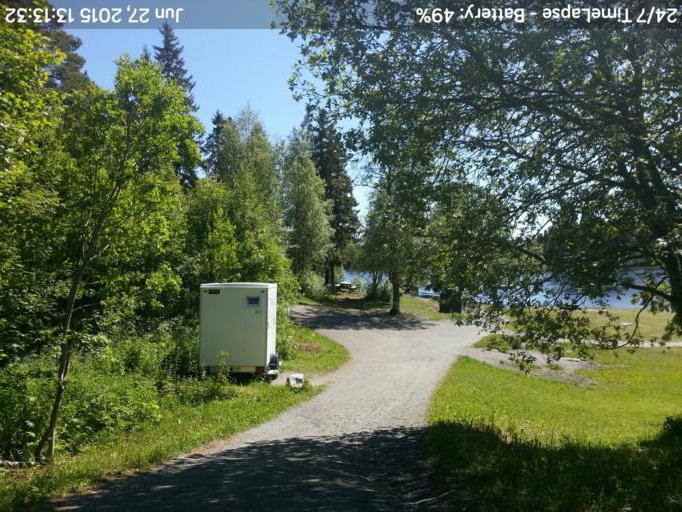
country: NO
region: Sor-Trondelag
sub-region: Trondheim
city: Trondheim
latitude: 63.4025
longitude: 10.3138
